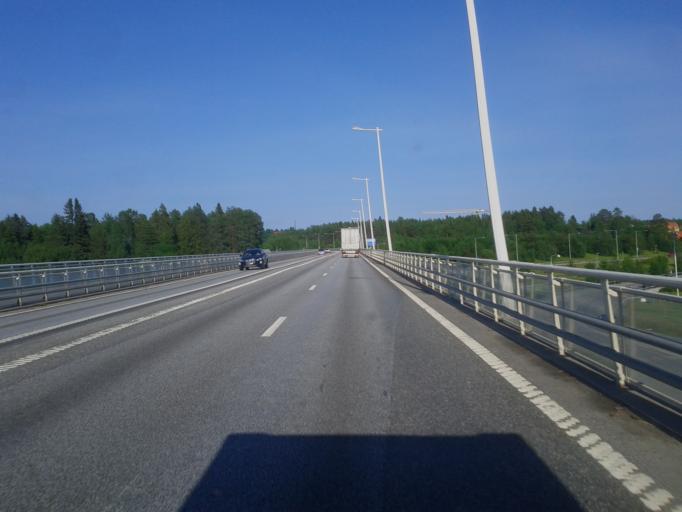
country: SE
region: Vaesterbotten
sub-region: Umea Kommun
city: Umea
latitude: 63.8012
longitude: 20.2987
